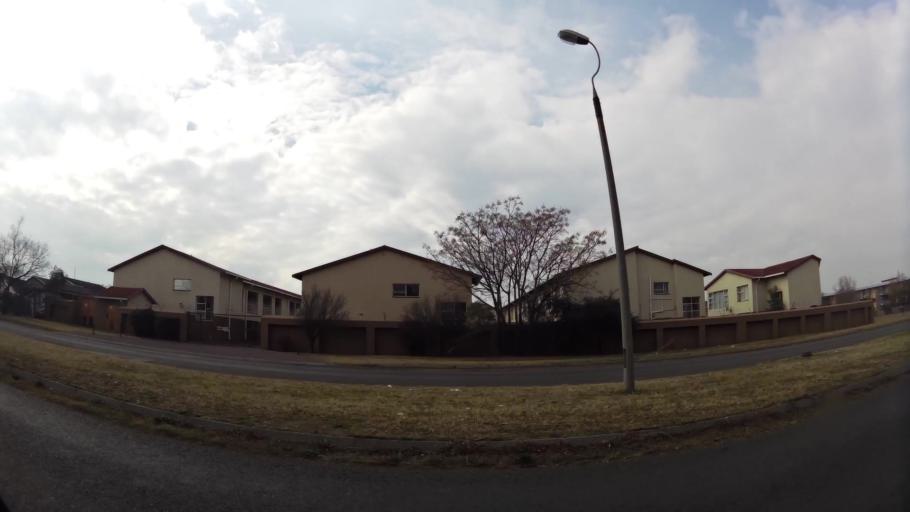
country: ZA
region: Gauteng
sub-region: Sedibeng District Municipality
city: Vanderbijlpark
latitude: -26.6956
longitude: 27.8474
